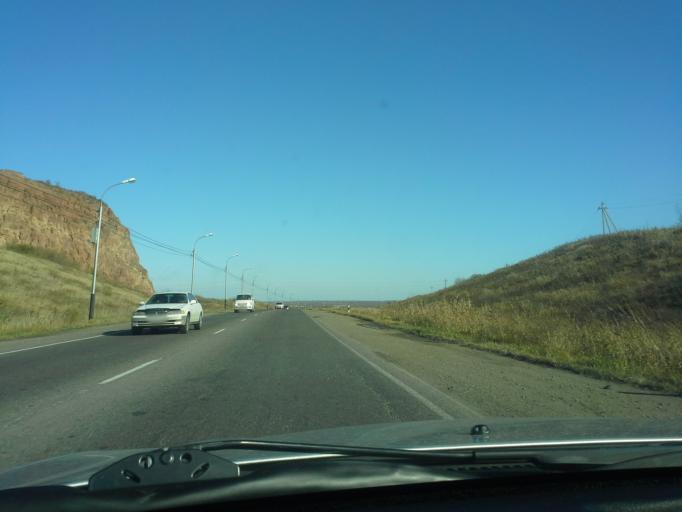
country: RU
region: Khabarovsk Krai
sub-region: Khabarovskiy Rayon
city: Khabarovsk
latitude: 48.5497
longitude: 135.0743
